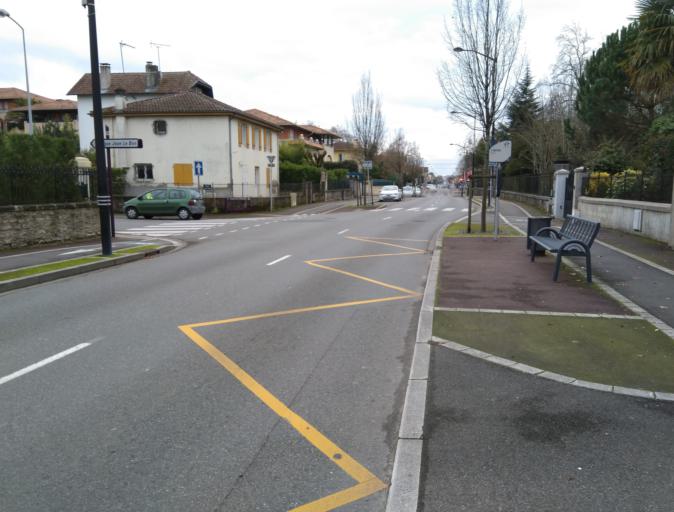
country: FR
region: Aquitaine
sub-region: Departement des Landes
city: Dax
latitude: 43.7036
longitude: -1.0621
